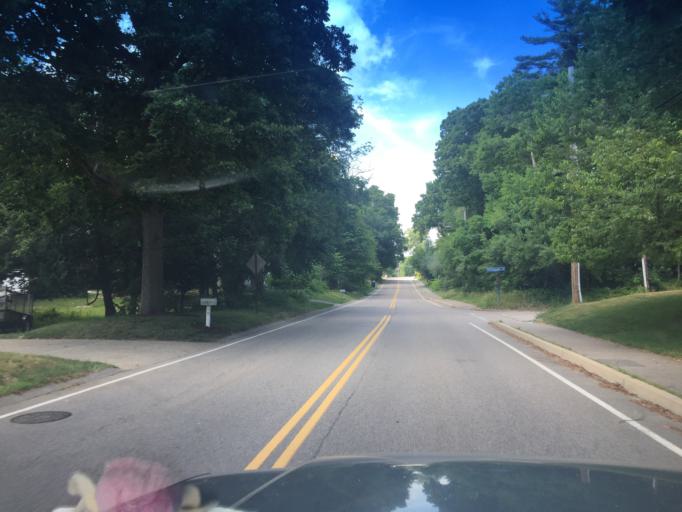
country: US
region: Massachusetts
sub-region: Norfolk County
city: Medway
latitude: 42.1544
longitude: -71.4199
